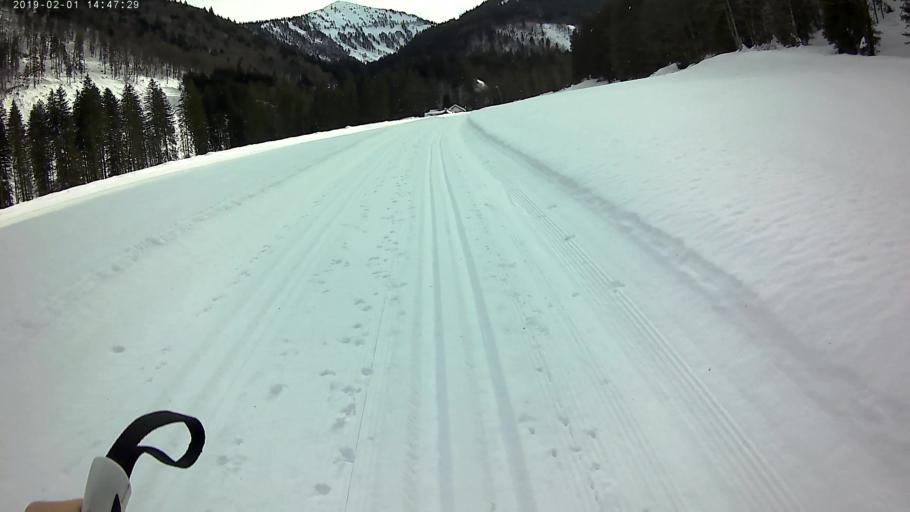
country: AT
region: Salzburg
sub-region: Politischer Bezirk Salzburg-Umgebung
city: Hintersee
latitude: 47.7113
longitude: 13.2853
